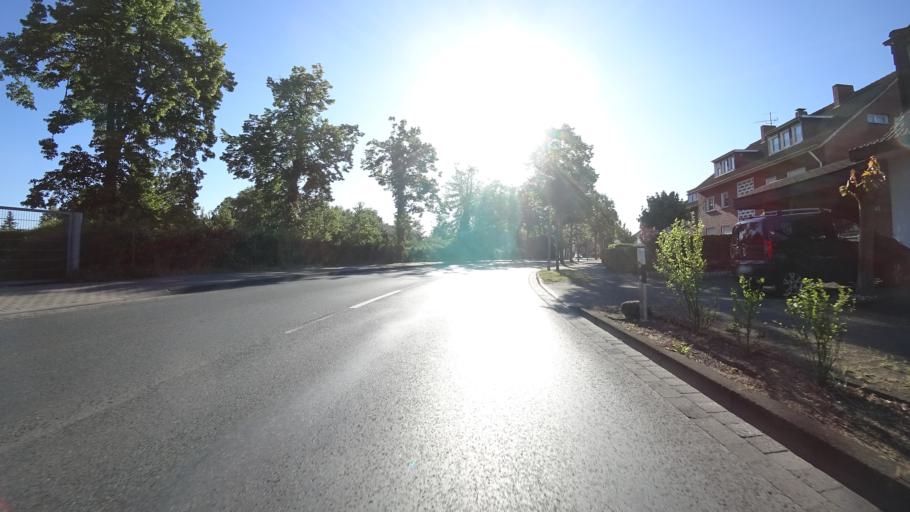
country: DE
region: North Rhine-Westphalia
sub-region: Regierungsbezirk Detmold
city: Rheda-Wiedenbruck
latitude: 51.8491
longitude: 8.2839
